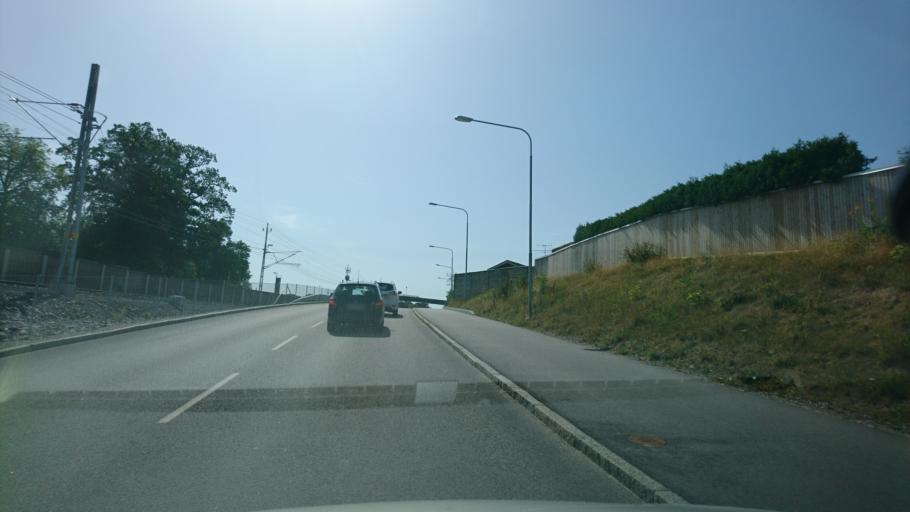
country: SE
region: Soedermanland
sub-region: Strangnas Kommun
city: Strangnas
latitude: 59.3657
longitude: 17.0374
